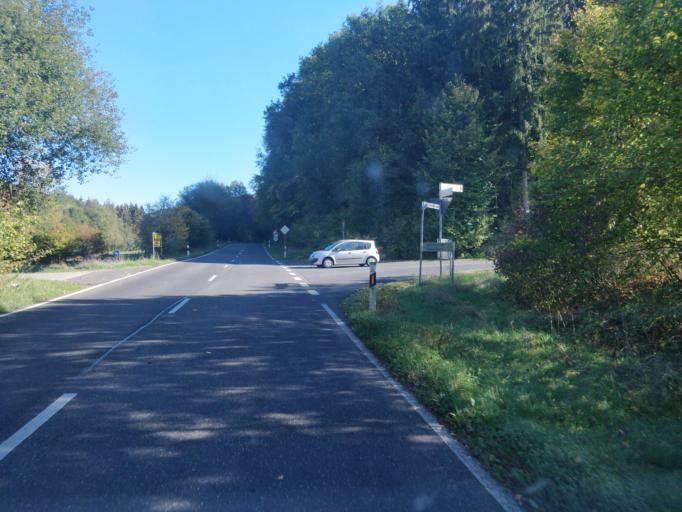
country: DE
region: North Rhine-Westphalia
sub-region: Regierungsbezirk Koln
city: Bad Munstereifel
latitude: 50.5603
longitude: 6.7796
